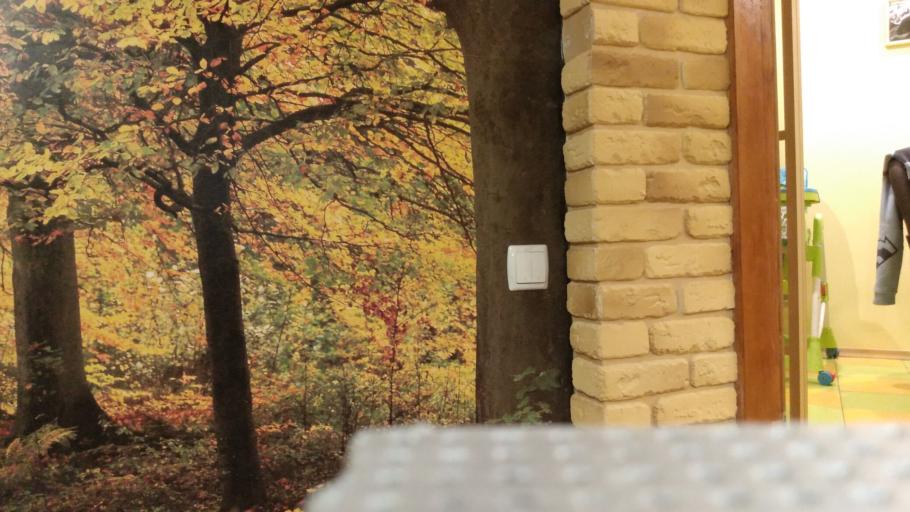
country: RU
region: Vologda
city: Babayevo
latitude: 59.3721
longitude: 35.9938
